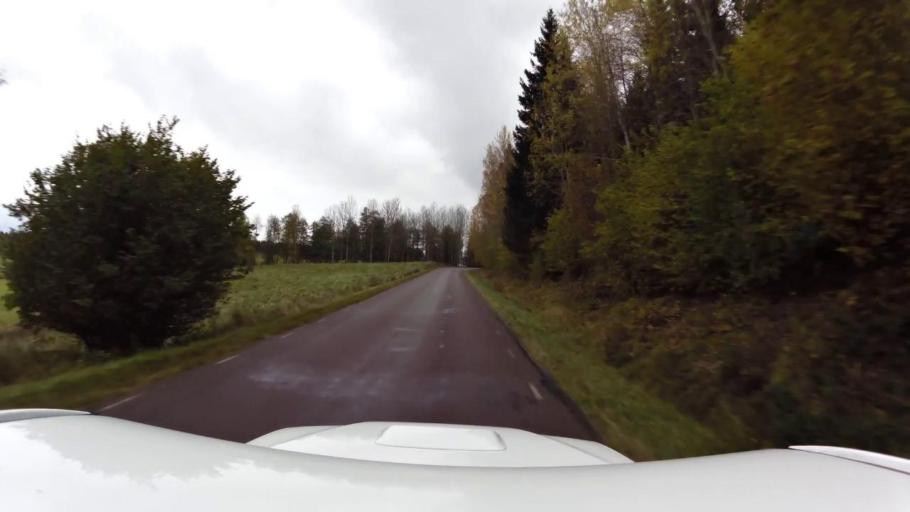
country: SE
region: OEstergoetland
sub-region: Linkopings Kommun
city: Ljungsbro
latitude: 58.5507
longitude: 15.5230
